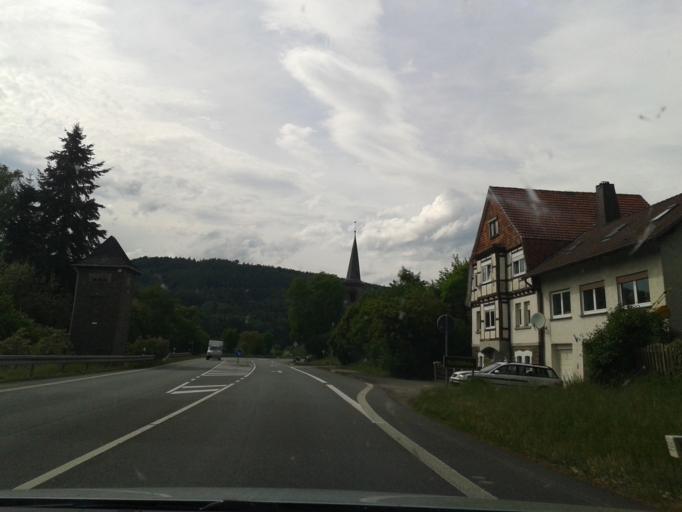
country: DE
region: Hesse
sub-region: Regierungsbezirk Kassel
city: Vohl
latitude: 51.1679
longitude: 8.8980
